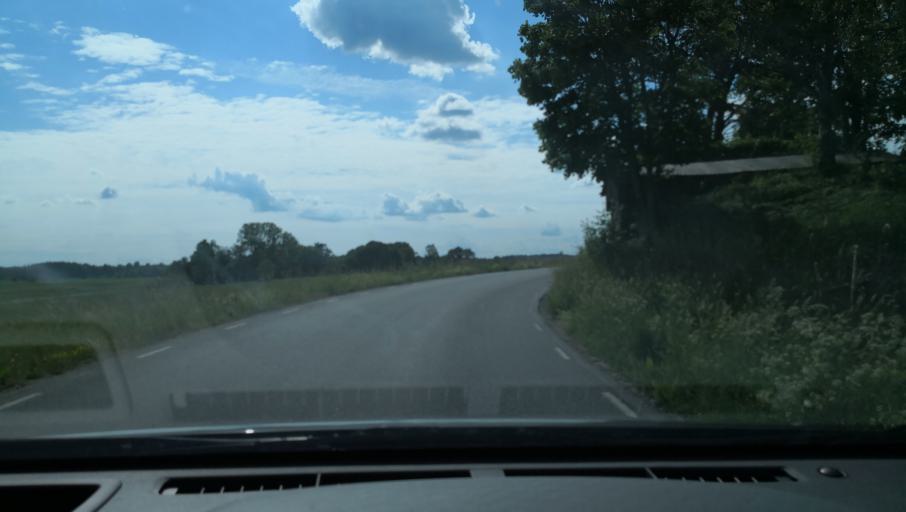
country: SE
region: Uppsala
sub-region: Enkopings Kommun
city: Orsundsbro
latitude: 59.8155
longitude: 17.3453
